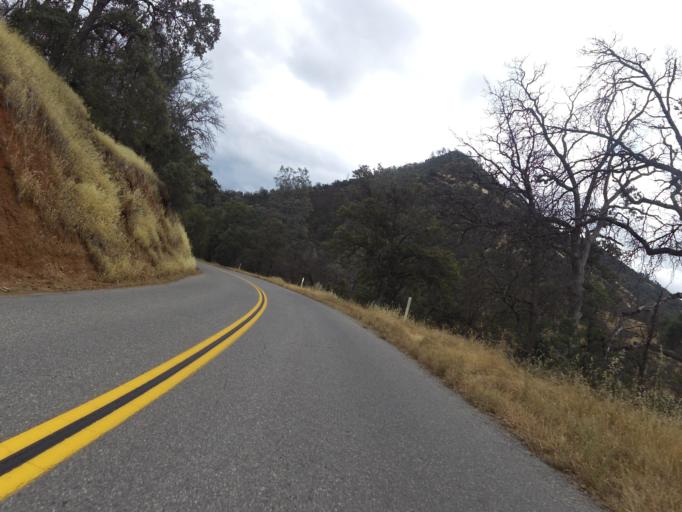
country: US
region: California
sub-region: Madera County
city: Ahwahnee
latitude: 37.3479
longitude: -119.7557
